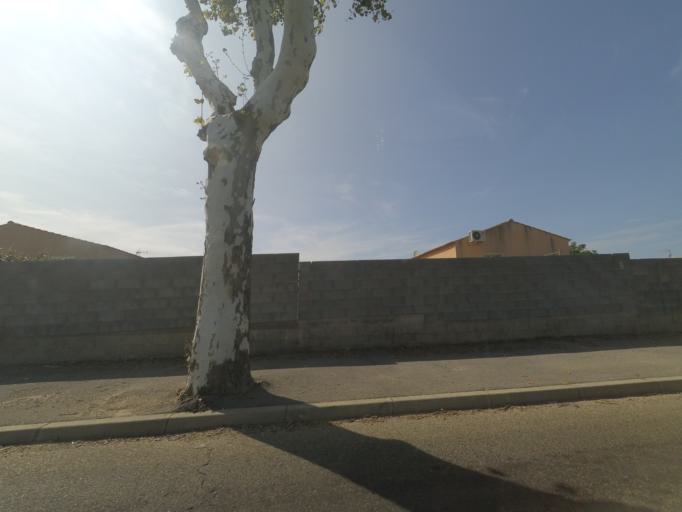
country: FR
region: Languedoc-Roussillon
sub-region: Departement du Gard
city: Villevieille
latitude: 43.8172
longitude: 4.1242
